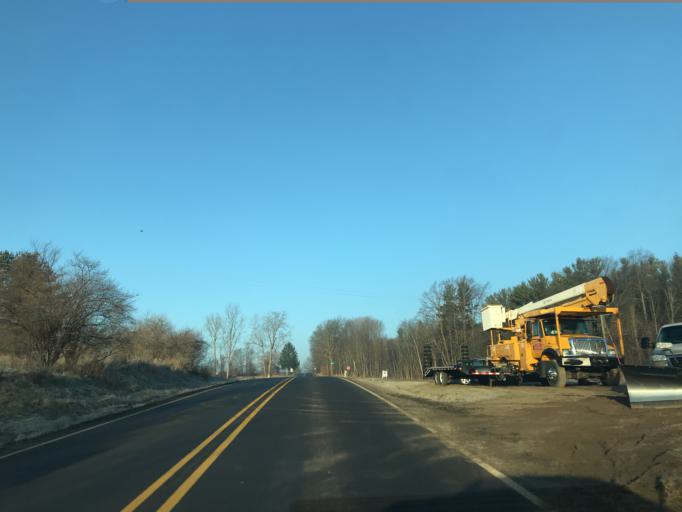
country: US
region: Michigan
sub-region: Ingham County
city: Leslie
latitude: 42.4358
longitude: -84.5397
